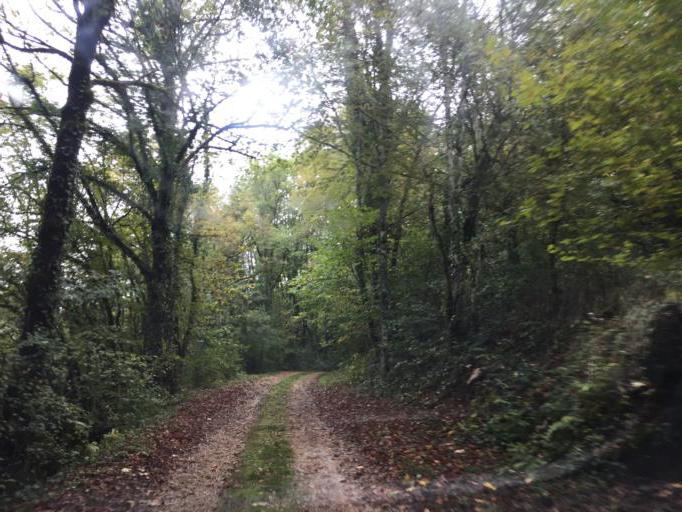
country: FR
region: Franche-Comte
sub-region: Departement du Jura
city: Orgelet
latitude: 46.5560
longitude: 5.6359
